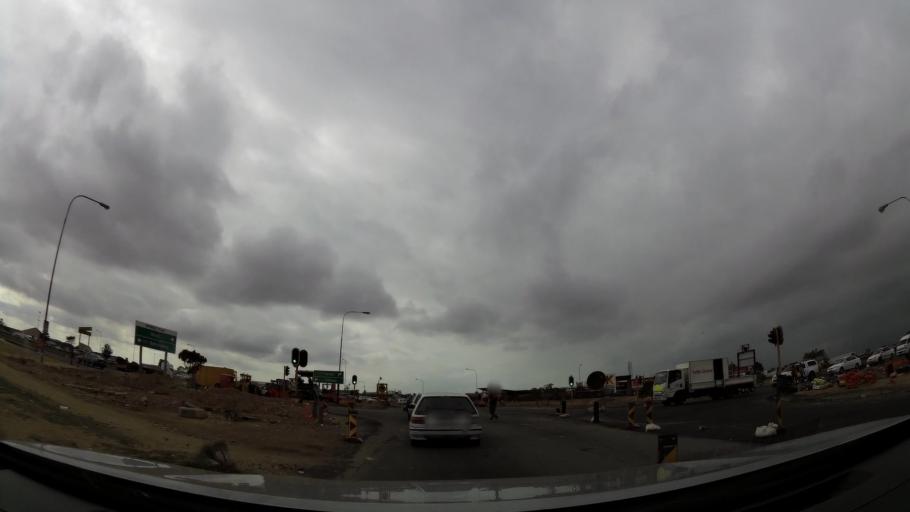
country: ZA
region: Eastern Cape
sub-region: Nelson Mandela Bay Metropolitan Municipality
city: Port Elizabeth
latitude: -33.8856
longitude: 25.5603
